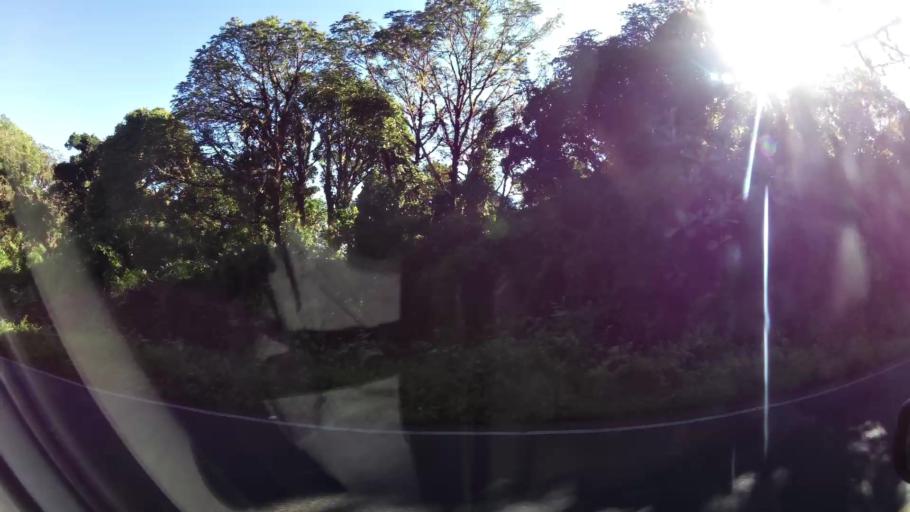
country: CR
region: San Jose
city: San Marcos
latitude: 9.7059
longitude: -83.9470
